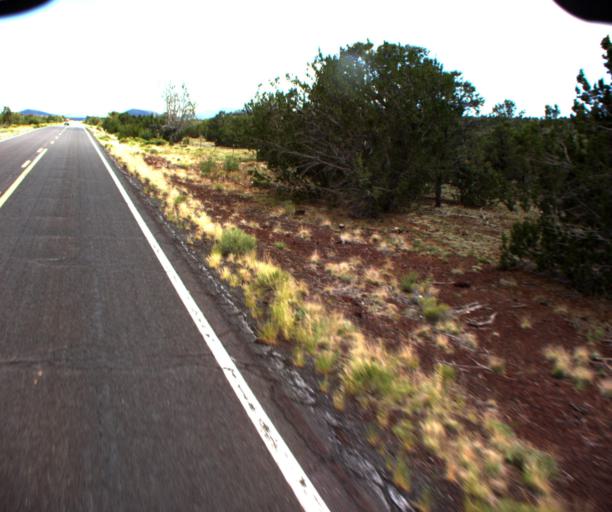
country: US
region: Arizona
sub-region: Coconino County
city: Parks
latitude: 35.5581
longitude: -111.8759
